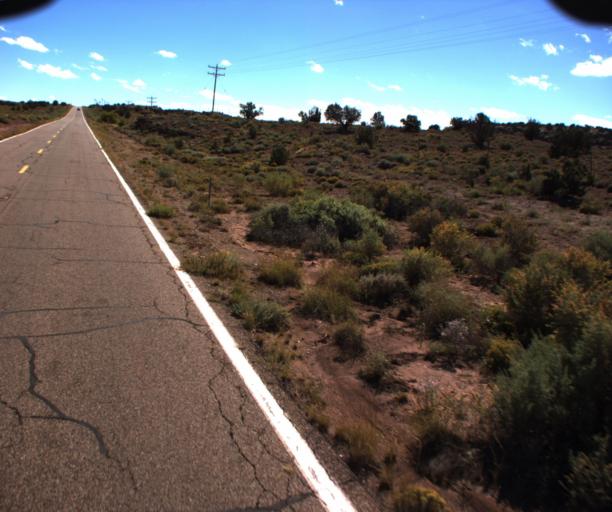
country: US
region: Arizona
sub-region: Apache County
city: Saint Johns
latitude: 34.5463
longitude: -109.6232
